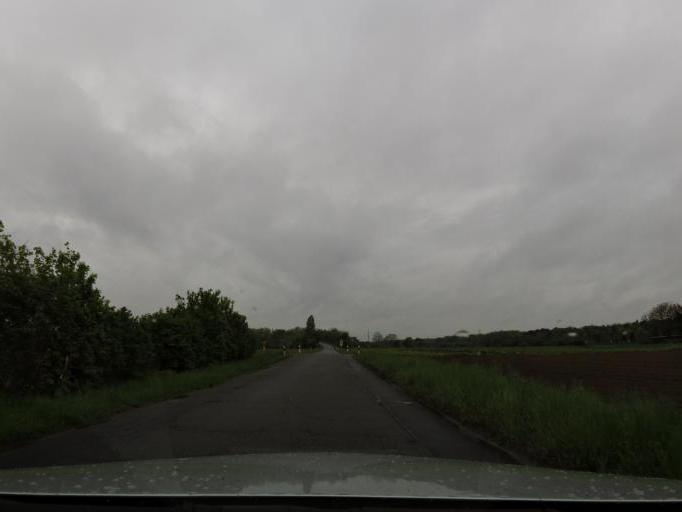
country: DE
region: Hesse
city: Griesheim
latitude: 49.8804
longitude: 8.5717
